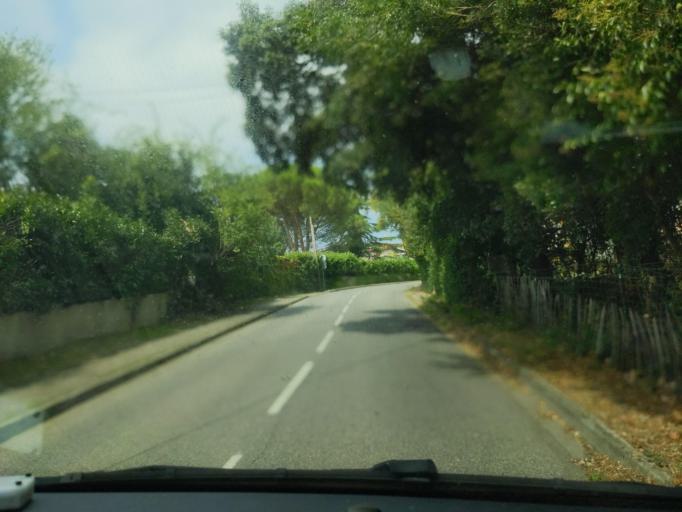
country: FR
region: Midi-Pyrenees
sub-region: Departement de la Haute-Garonne
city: Saint-Orens-de-Gameville
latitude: 43.5455
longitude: 1.5334
